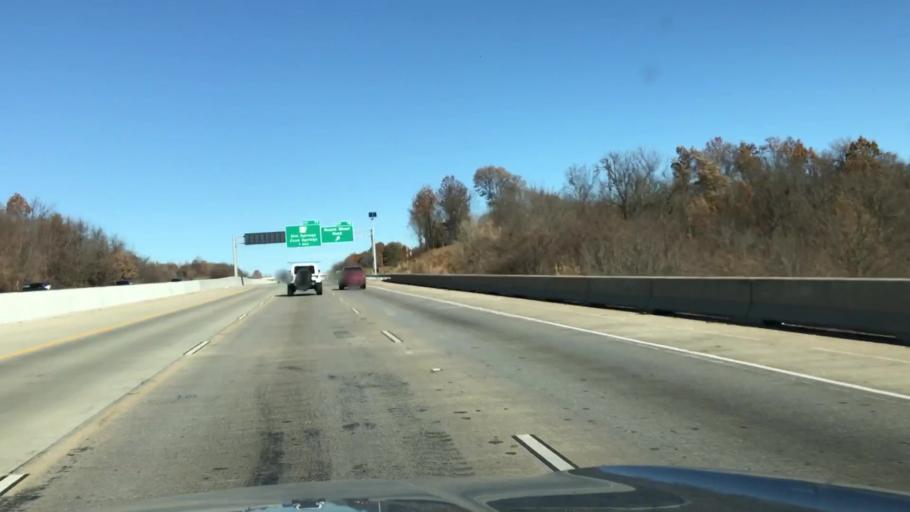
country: US
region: Arkansas
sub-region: Benton County
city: Bethel Heights
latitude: 36.2202
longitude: -94.1805
